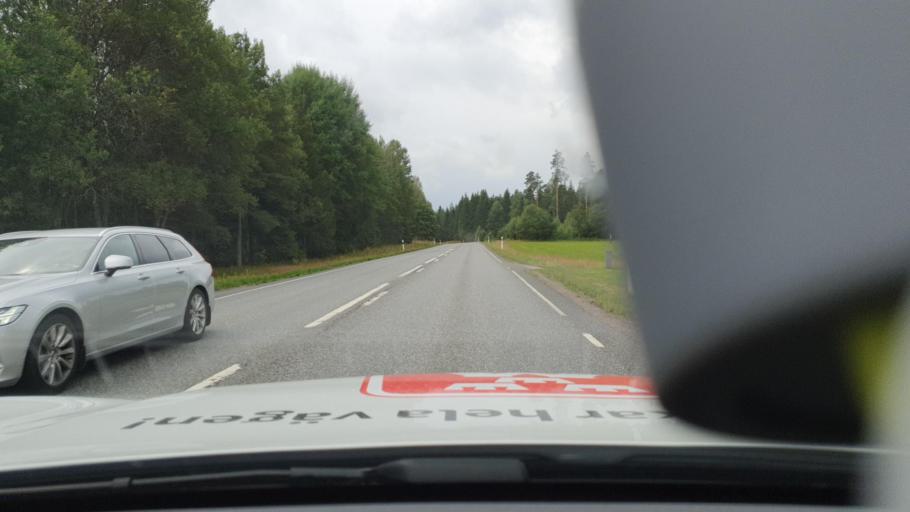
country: SE
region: Joenkoeping
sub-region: Gislaveds Kommun
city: Smalandsstenar
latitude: 57.1805
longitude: 13.4267
